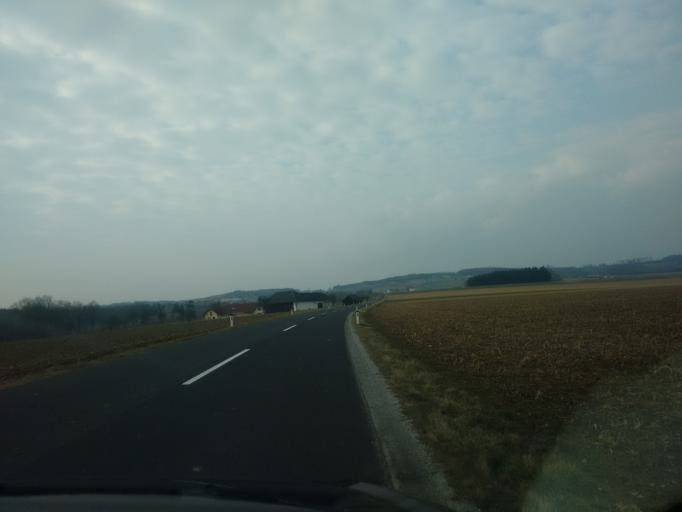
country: AT
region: Upper Austria
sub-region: Wels-Land
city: Holzhausen
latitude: 48.2230
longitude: 14.0742
